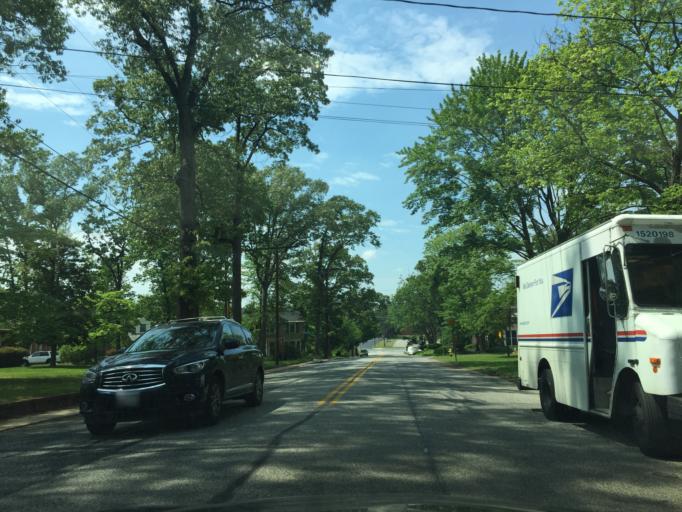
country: US
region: Maryland
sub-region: Anne Arundel County
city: Glen Burnie
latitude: 39.1681
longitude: -76.6313
